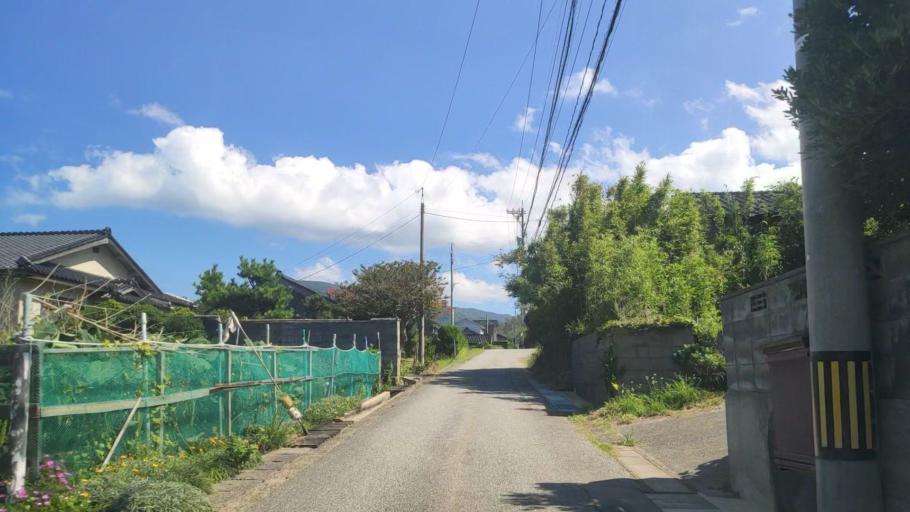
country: JP
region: Ishikawa
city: Nanao
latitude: 37.4486
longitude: 137.0569
